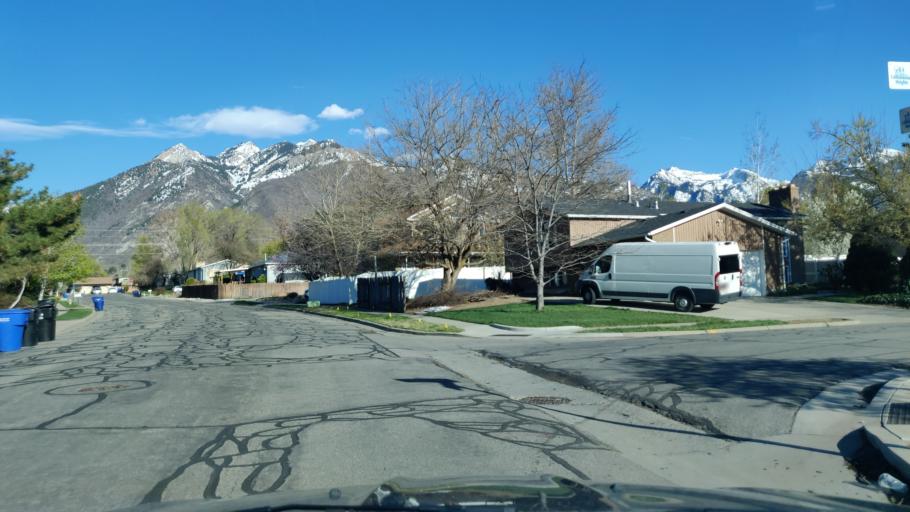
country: US
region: Utah
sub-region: Salt Lake County
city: Cottonwood Heights
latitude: 40.6181
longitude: -111.8174
